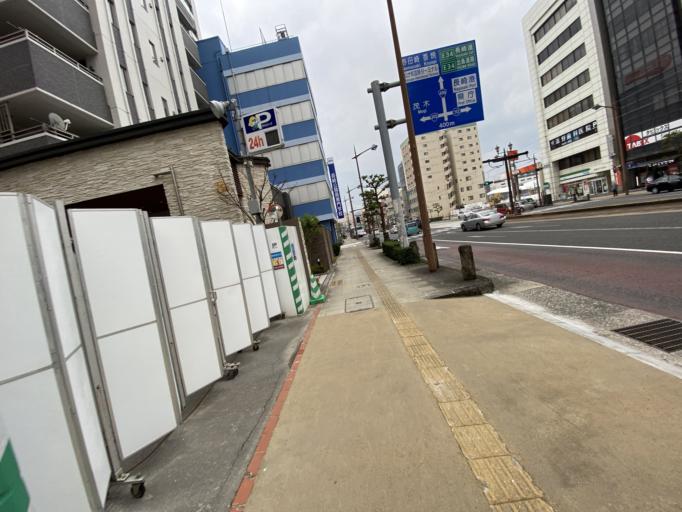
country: JP
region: Nagasaki
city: Nagasaki-shi
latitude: 32.7500
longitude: 129.8723
